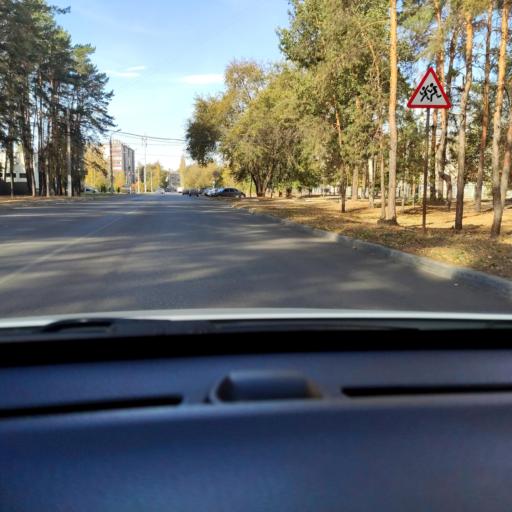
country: RU
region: Voronezj
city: Pridonskoy
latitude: 51.6811
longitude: 39.0914
